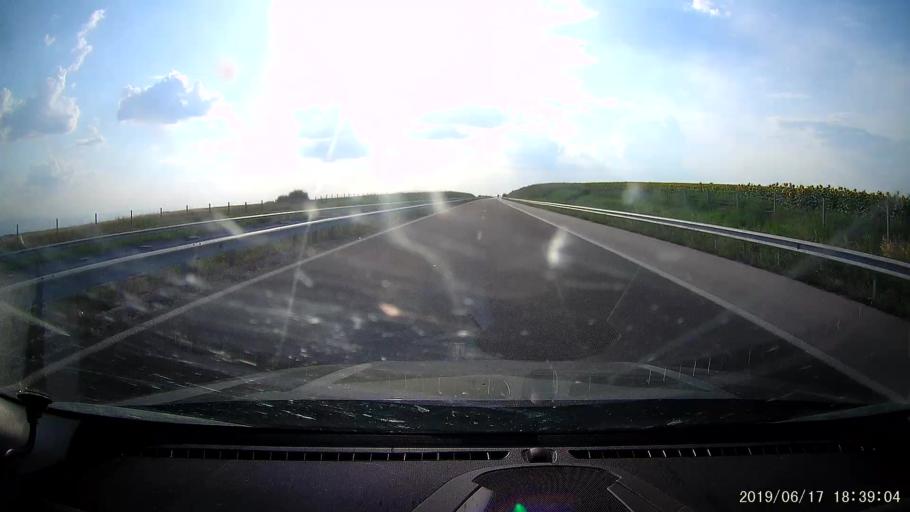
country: BG
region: Stara Zagora
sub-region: Obshtina Chirpan
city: Chirpan
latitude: 42.1417
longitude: 25.3181
